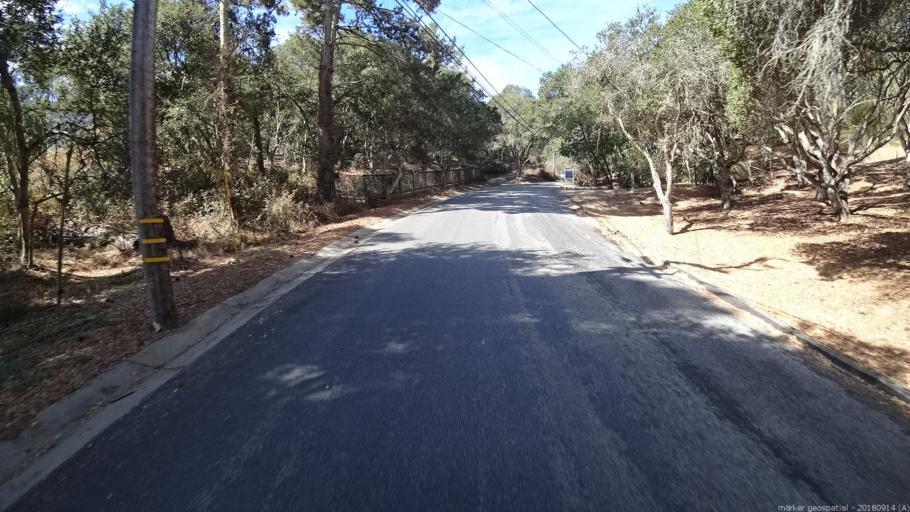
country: US
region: California
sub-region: San Benito County
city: Aromas
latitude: 36.8774
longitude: -121.6450
